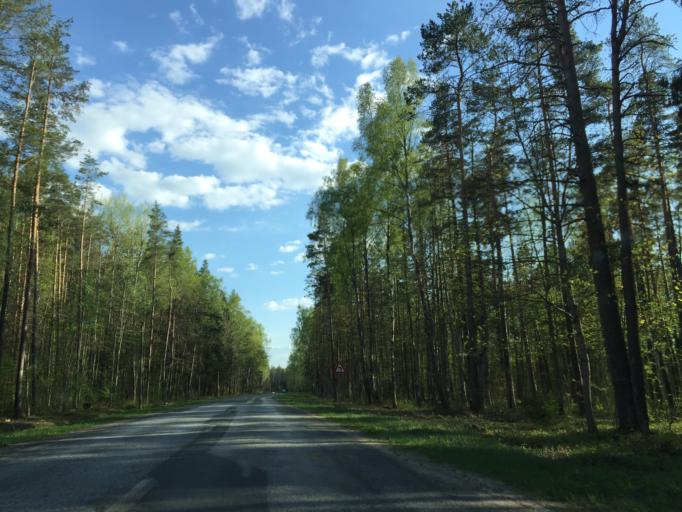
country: LV
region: Sigulda
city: Sigulda
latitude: 57.2346
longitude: 24.8522
